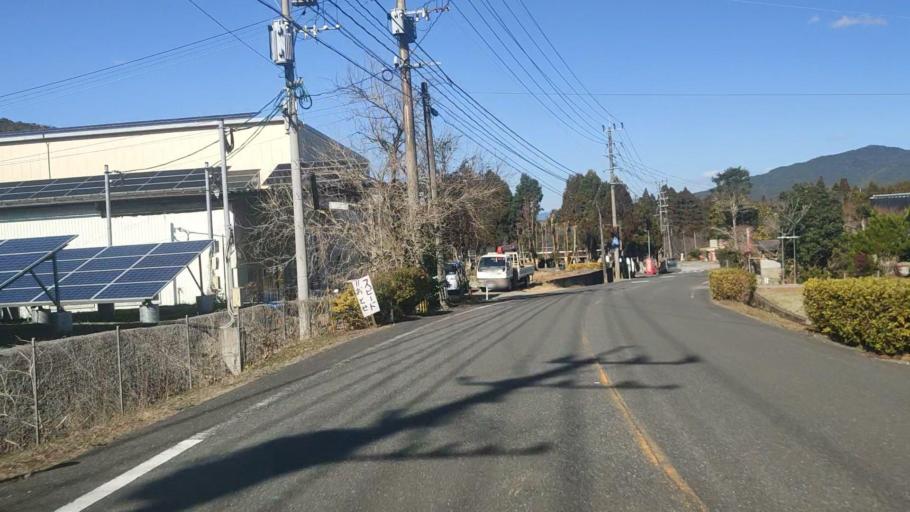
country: JP
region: Oita
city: Saiki
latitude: 32.9024
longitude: 131.9334
